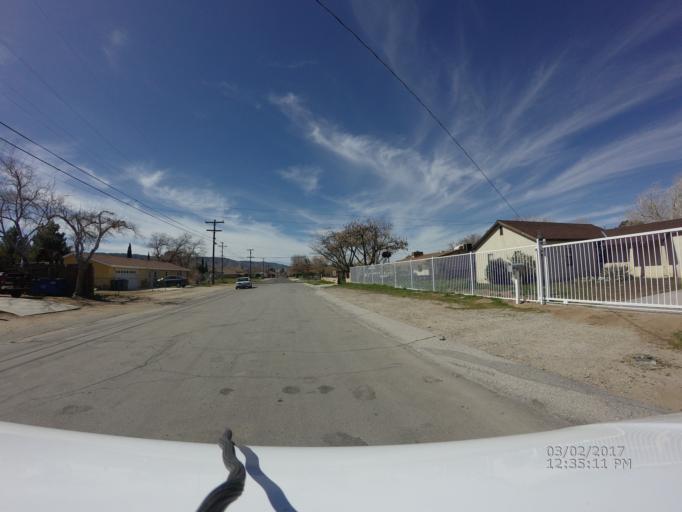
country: US
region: California
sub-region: Los Angeles County
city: Quartz Hill
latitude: 34.6511
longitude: -118.2223
